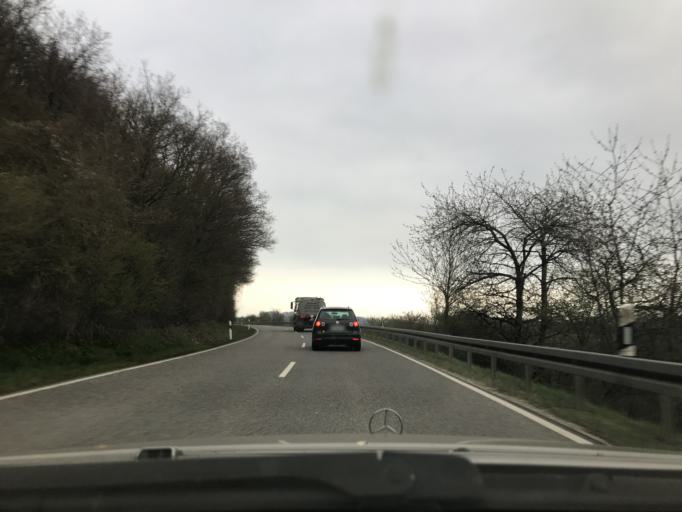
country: DE
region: Thuringia
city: Geisleden
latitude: 51.3468
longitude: 10.2100
